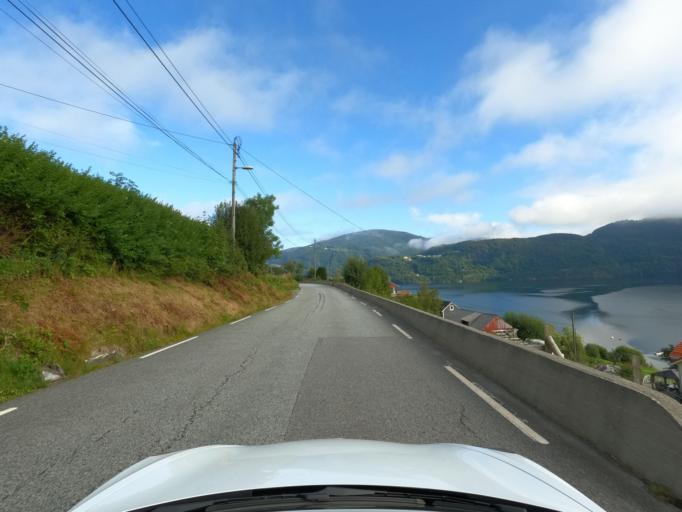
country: NO
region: Hordaland
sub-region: Bergen
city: Indre Arna
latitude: 60.4288
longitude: 5.4989
